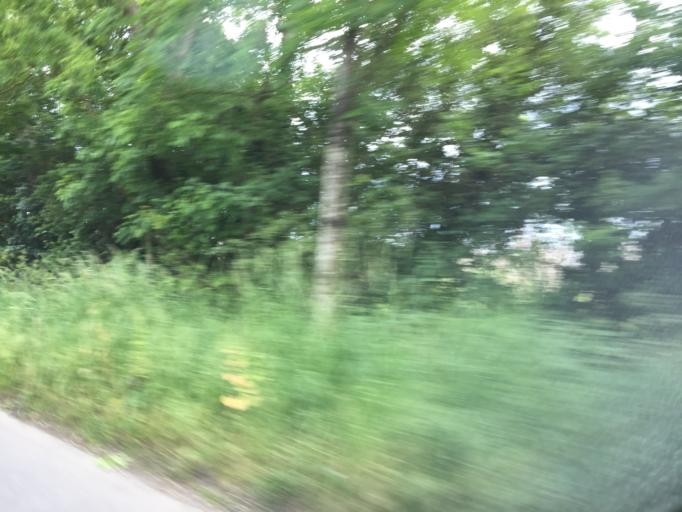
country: GB
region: England
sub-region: Wiltshire
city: Leigh
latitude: 51.6354
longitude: -1.8929
